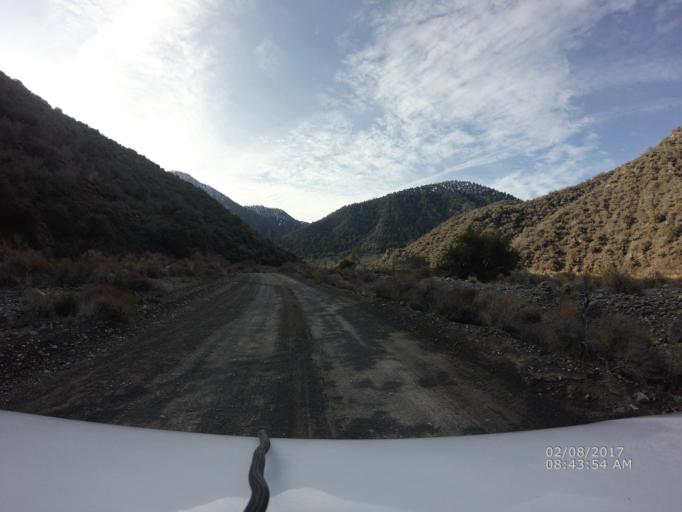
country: US
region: California
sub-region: San Bernardino County
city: Pinon Hills
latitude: 34.4042
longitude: -117.8241
